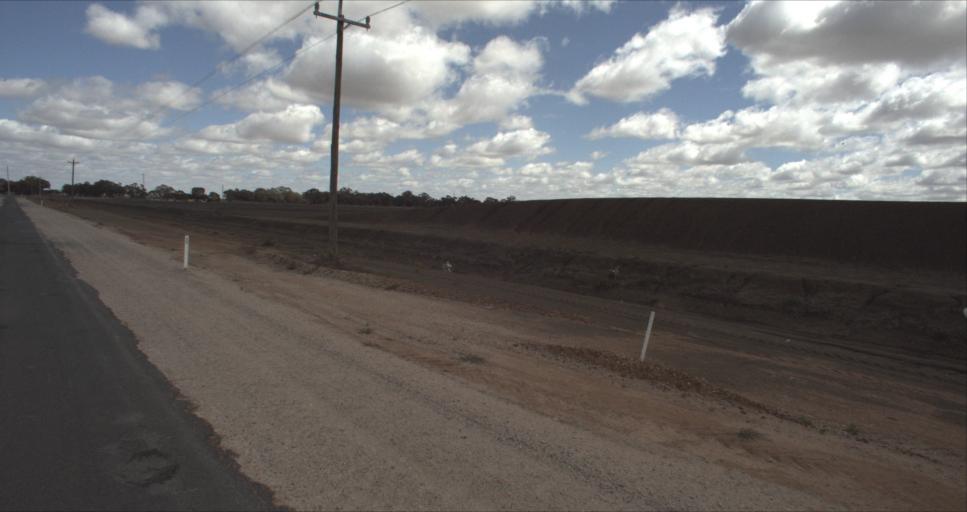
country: AU
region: New South Wales
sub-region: Murrumbidgee Shire
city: Darlington Point
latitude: -34.5752
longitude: 146.1710
